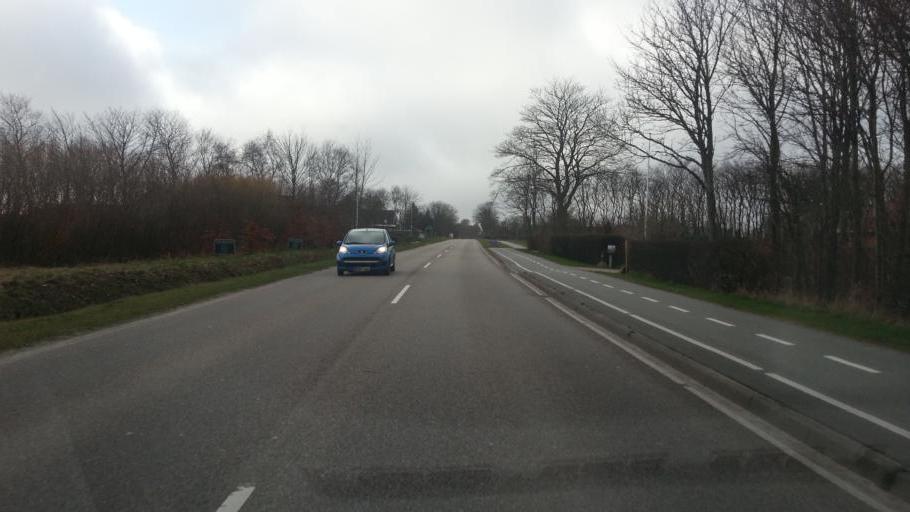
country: DK
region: South Denmark
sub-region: Varde Kommune
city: Oksbol
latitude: 55.6211
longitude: 8.2996
